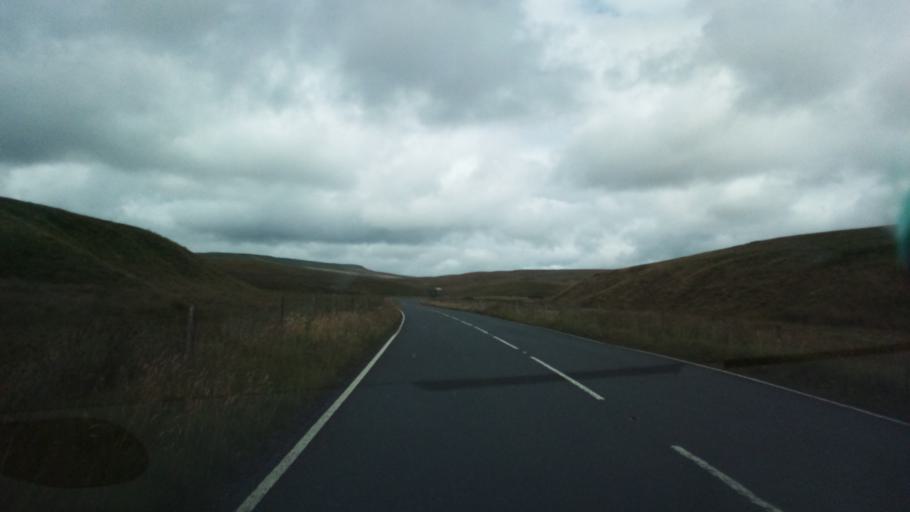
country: GB
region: England
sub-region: North Yorkshire
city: Settle
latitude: 54.2305
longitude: -2.3191
